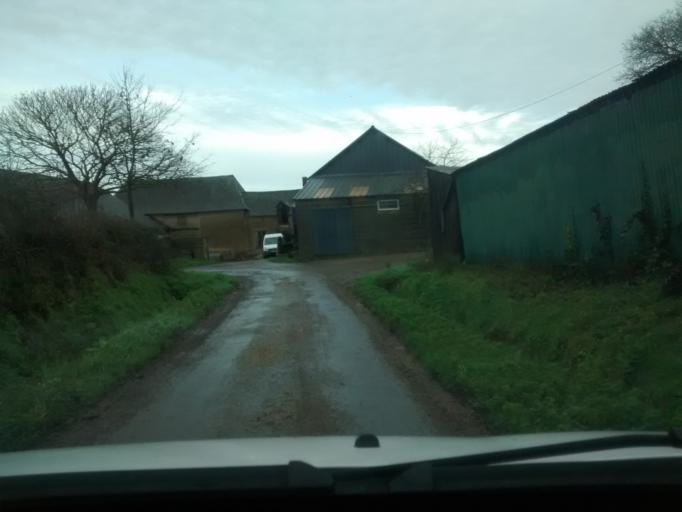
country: FR
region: Brittany
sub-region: Departement d'Ille-et-Vilaine
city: Montgermont
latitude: 48.1368
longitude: -1.7078
